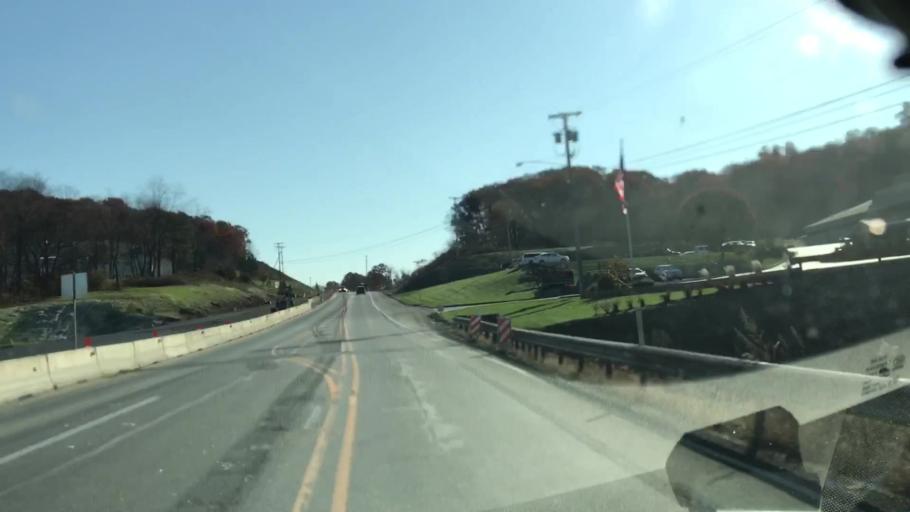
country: US
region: Pennsylvania
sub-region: Butler County
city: Mars
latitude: 40.6912
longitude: -80.0180
